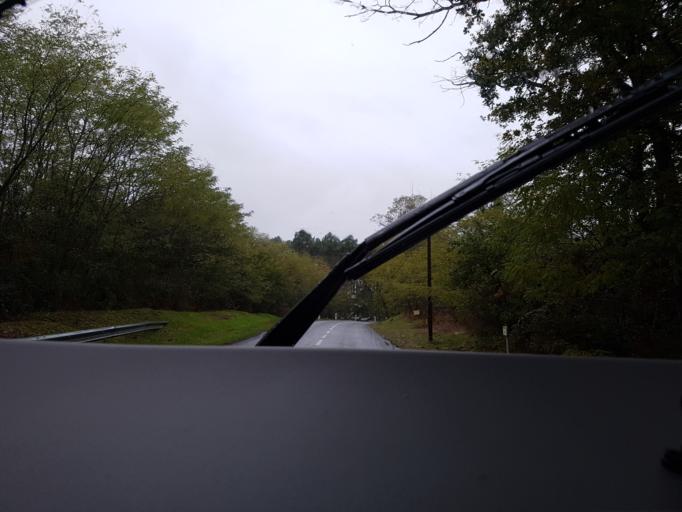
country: FR
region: Aquitaine
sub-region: Departement des Landes
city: Pissos
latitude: 44.3597
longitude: -0.6359
